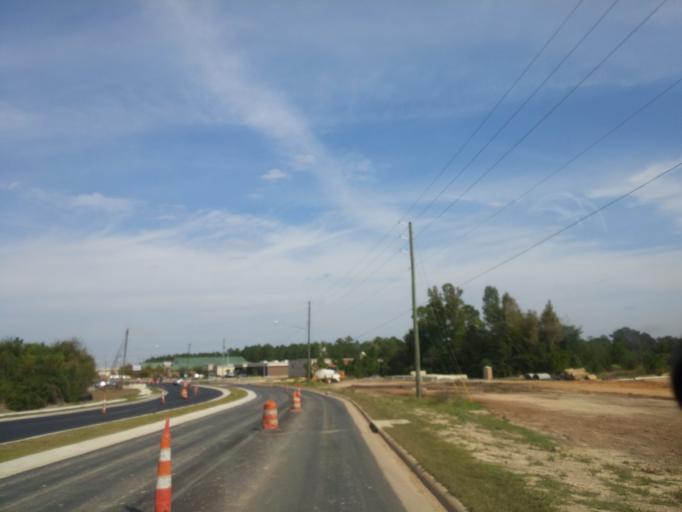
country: US
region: Mississippi
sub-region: Harrison County
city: West Gulfport
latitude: 30.4211
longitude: -89.0882
